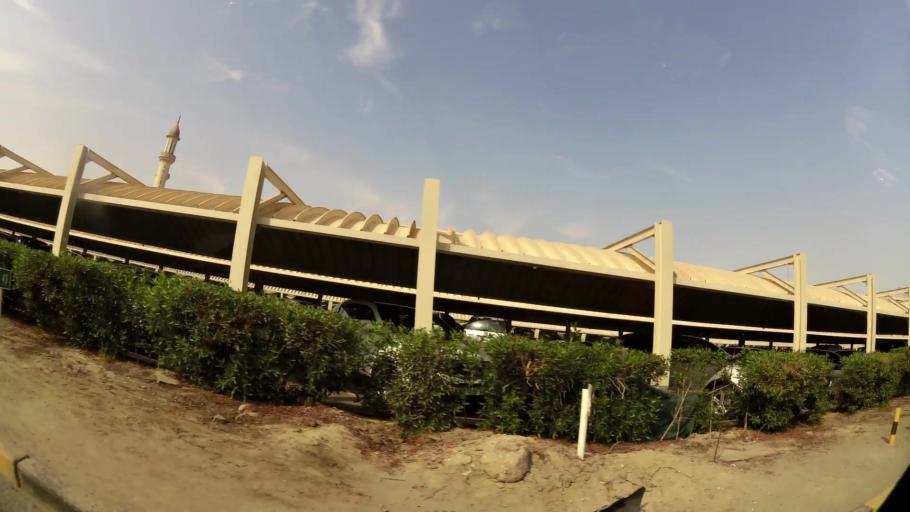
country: KW
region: Al Asimah
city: Ash Shamiyah
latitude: 29.3184
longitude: 47.9707
